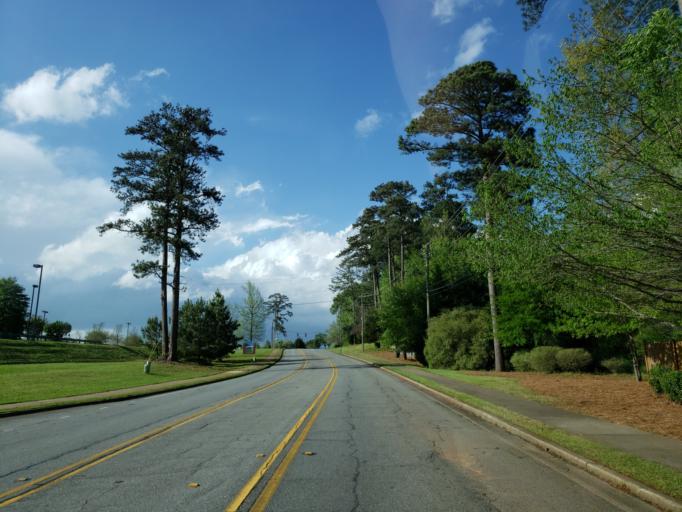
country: US
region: Georgia
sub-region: Fulton County
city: Roswell
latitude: 34.0570
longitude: -84.3346
